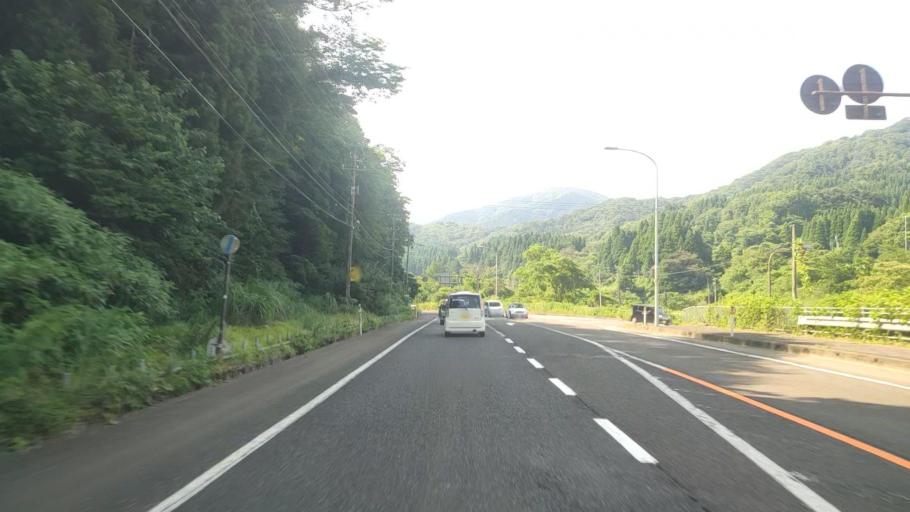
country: JP
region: Fukui
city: Tsuruga
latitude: 35.6067
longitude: 136.1213
